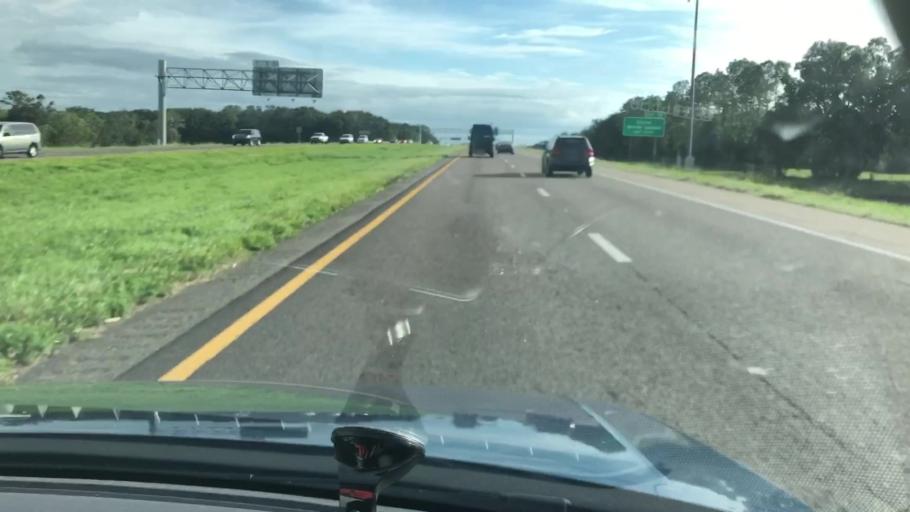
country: US
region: Florida
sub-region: Orange County
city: Ocoee
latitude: 28.5903
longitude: -81.5578
